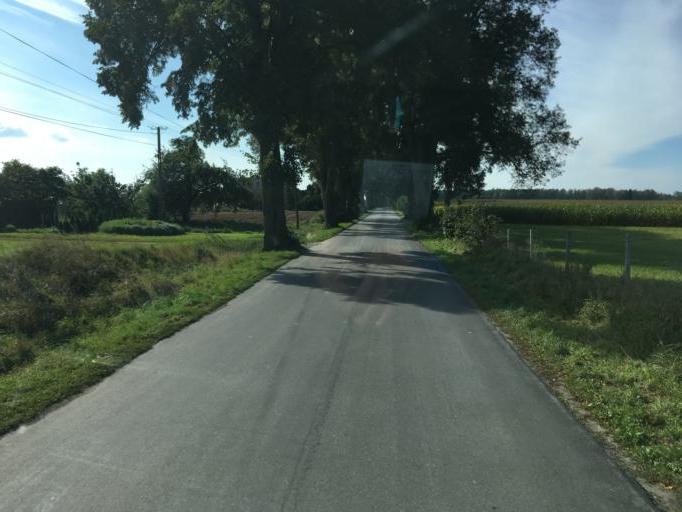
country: PL
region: Kujawsko-Pomorskie
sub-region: Powiat swiecki
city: Lniano
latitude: 53.5738
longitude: 18.2541
